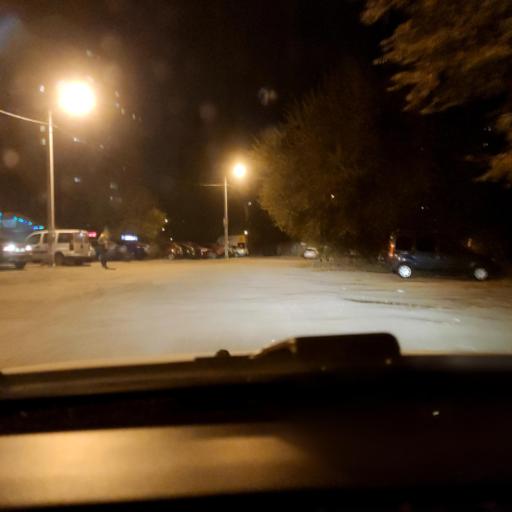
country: RU
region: Voronezj
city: Voronezh
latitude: 51.6878
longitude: 39.1977
